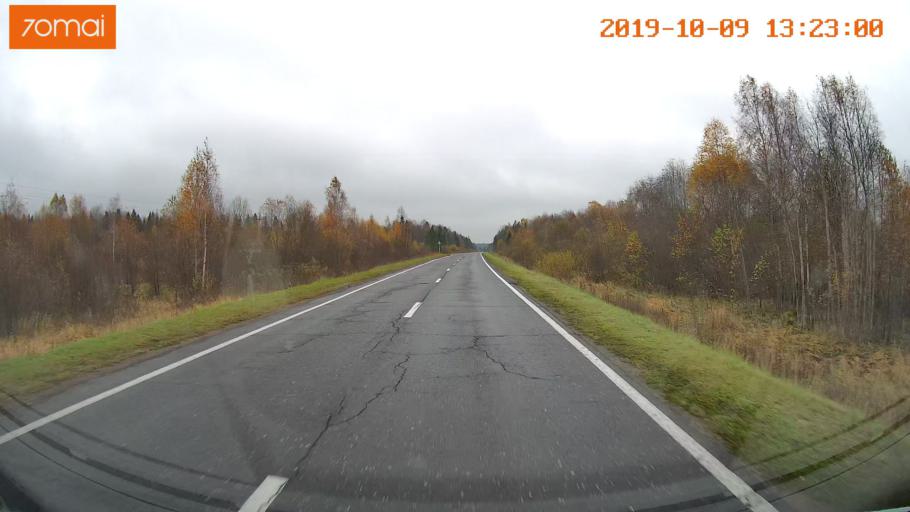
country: RU
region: Jaroslavl
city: Lyubim
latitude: 58.3374
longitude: 40.8781
